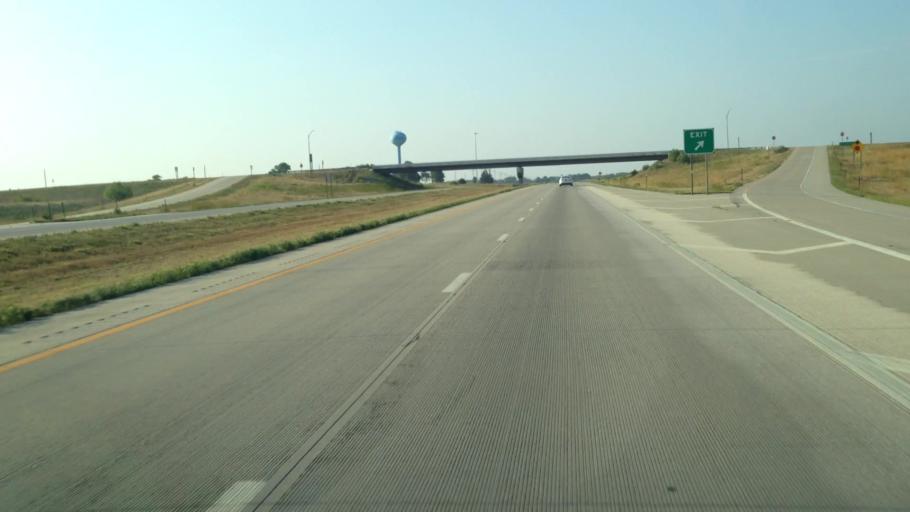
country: US
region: Kansas
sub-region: Douglas County
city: Baldwin City
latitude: 38.8307
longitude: -95.2689
